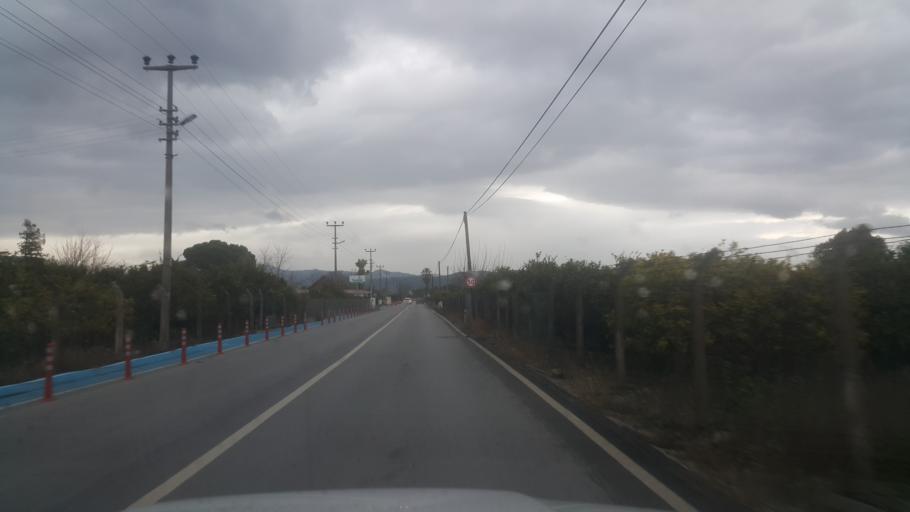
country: TR
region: Izmir
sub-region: Seferihisar
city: Seferhisar
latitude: 38.1897
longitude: 26.8131
